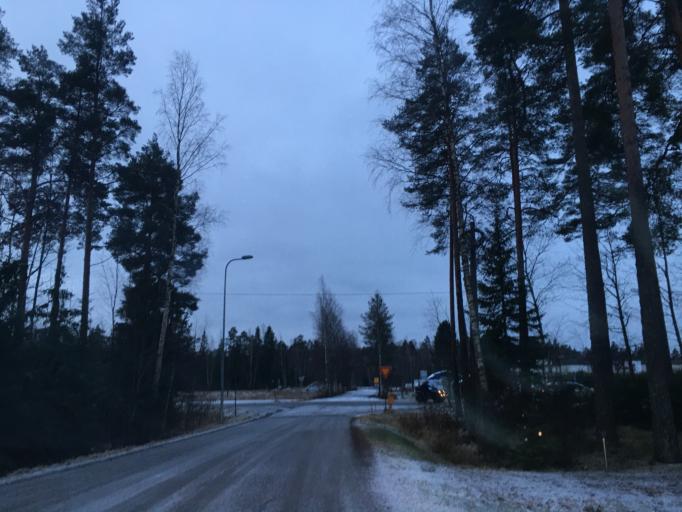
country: FI
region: Varsinais-Suomi
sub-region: Loimaa
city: Aura
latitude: 60.6450
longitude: 22.6079
